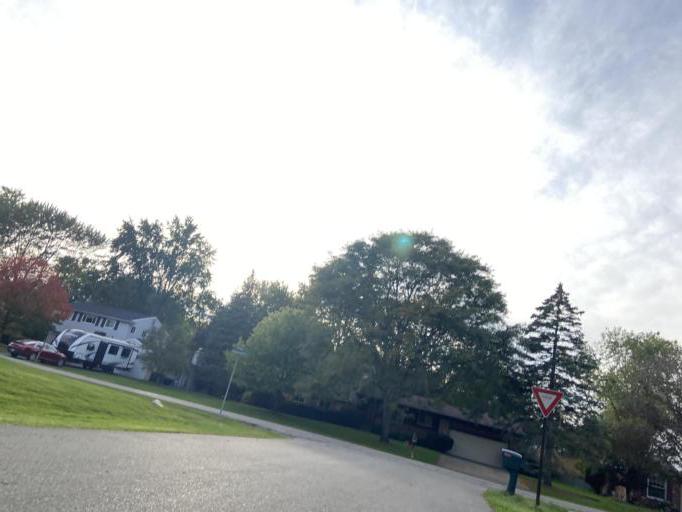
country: US
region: Michigan
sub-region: Oakland County
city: Farmington Hills
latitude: 42.5074
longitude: -83.3728
